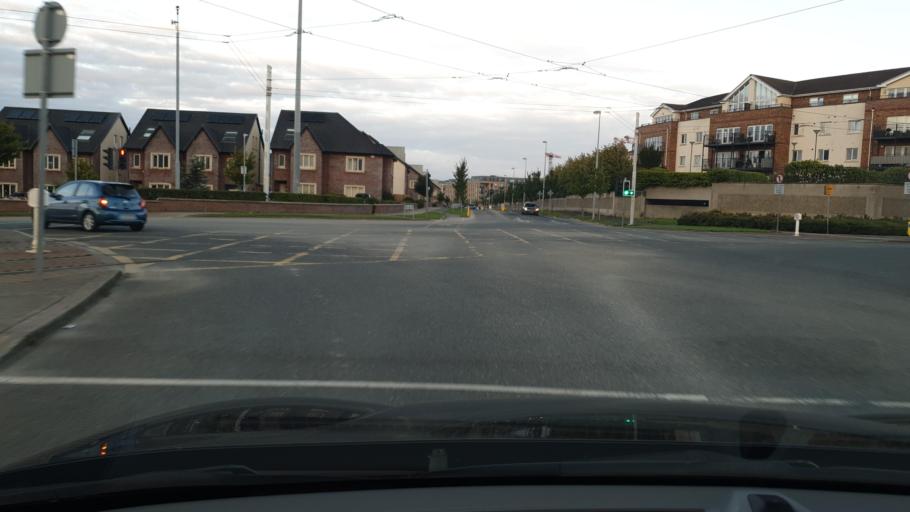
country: IE
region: Leinster
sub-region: South Dublin
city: Saggart
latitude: 53.2845
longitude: -6.4336
